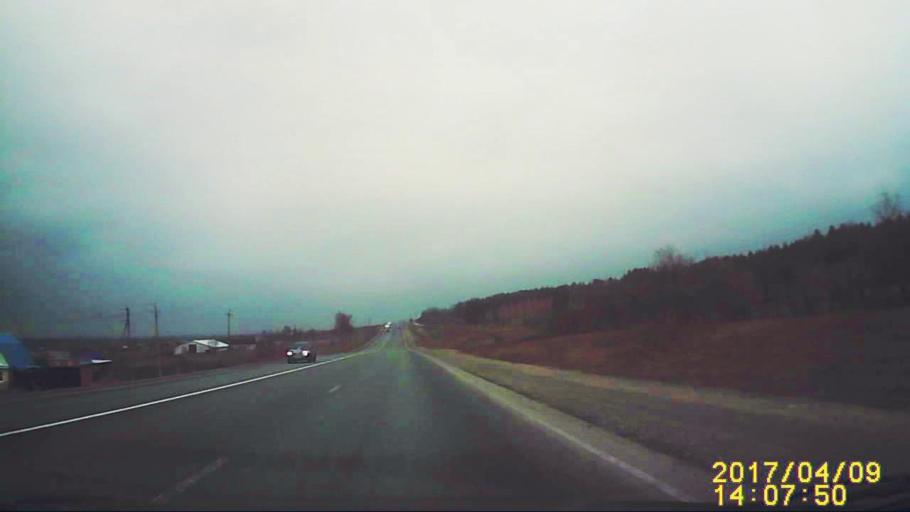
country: RU
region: Ulyanovsk
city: Silikatnyy
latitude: 54.0148
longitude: 48.2171
